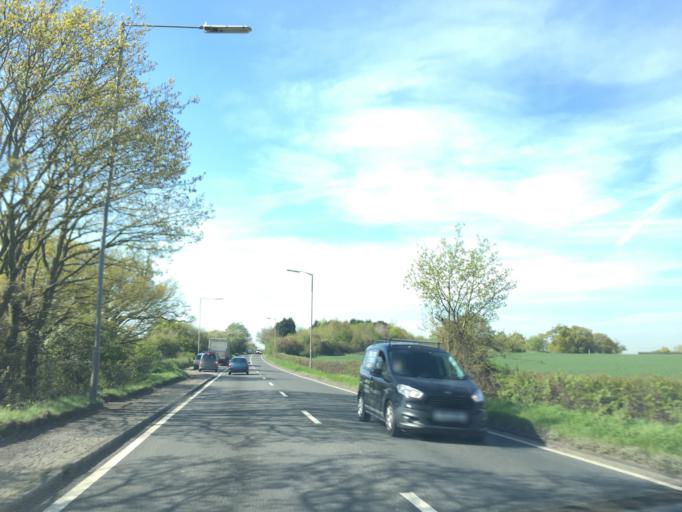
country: GB
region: England
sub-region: Essex
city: Harlow
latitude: 51.7390
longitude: 0.1309
